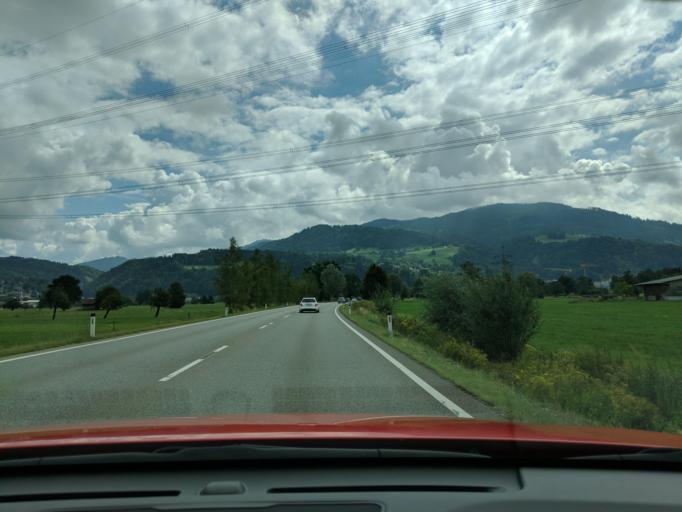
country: AT
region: Vorarlberg
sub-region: Politischer Bezirk Bregenz
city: Schwarzach
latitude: 47.4428
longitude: 9.7387
